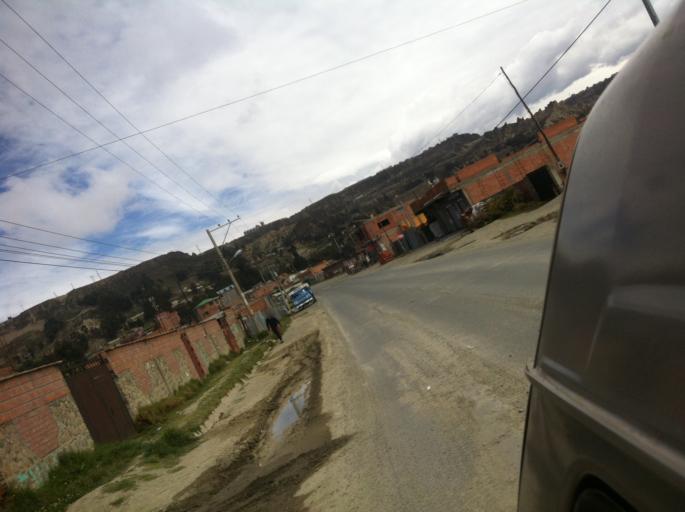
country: BO
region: La Paz
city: La Paz
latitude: -16.5756
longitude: -68.1695
